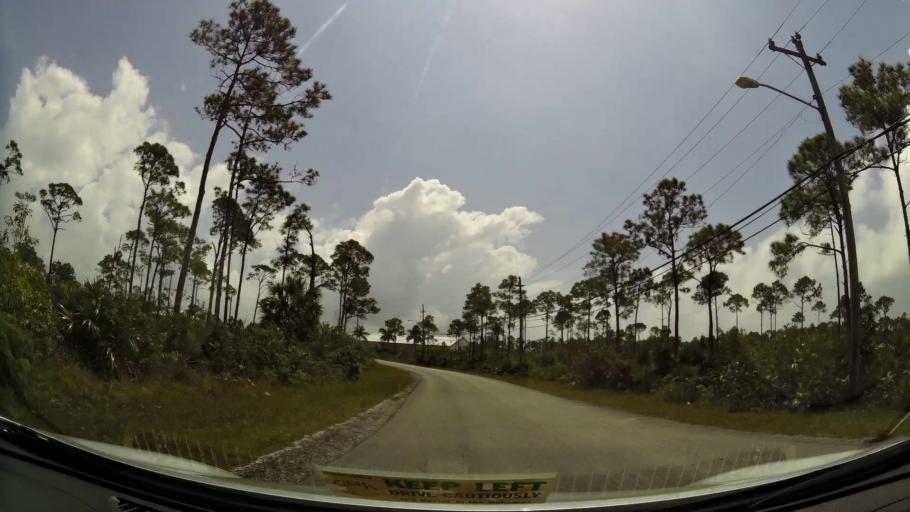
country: BS
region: Freeport
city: Lucaya
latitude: 26.5255
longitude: -78.6322
